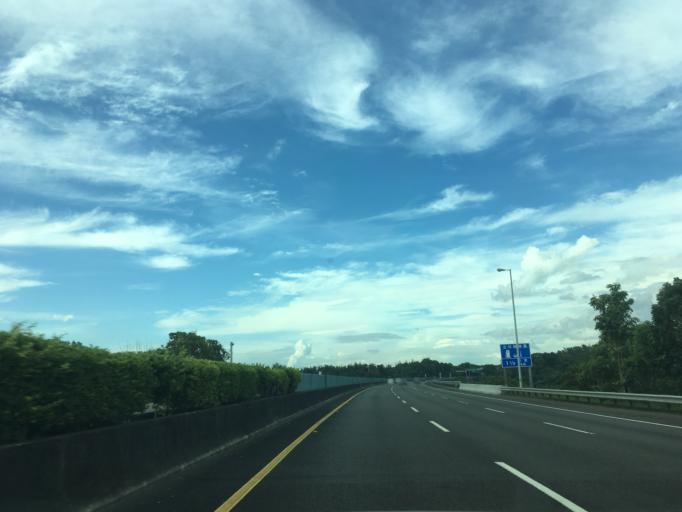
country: TW
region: Taiwan
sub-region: Yunlin
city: Douliu
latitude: 23.6013
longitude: 120.5264
